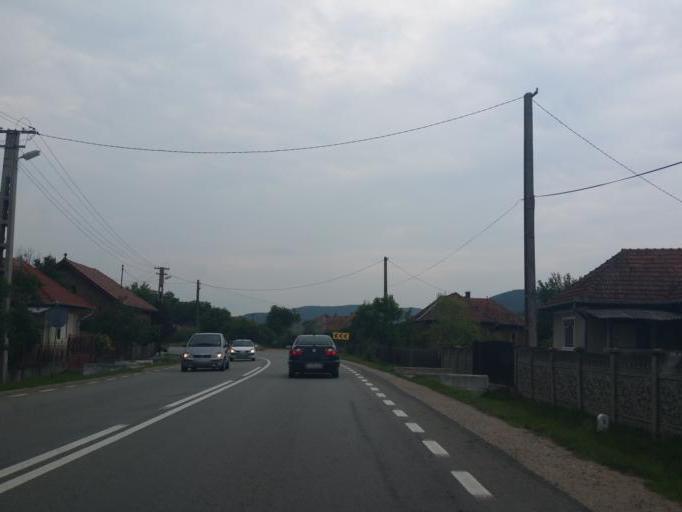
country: RO
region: Salaj
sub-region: Comuna Sanmihaiu Almasului
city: Sanmihaiu Almasului
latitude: 46.9594
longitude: 23.3307
